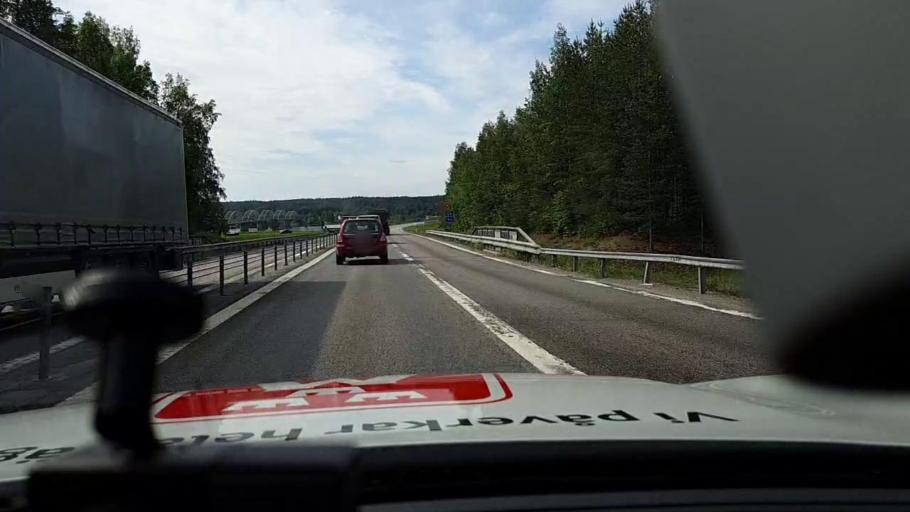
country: SE
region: Norrbotten
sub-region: Lulea Kommun
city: Gammelstad
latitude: 65.5965
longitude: 22.0420
